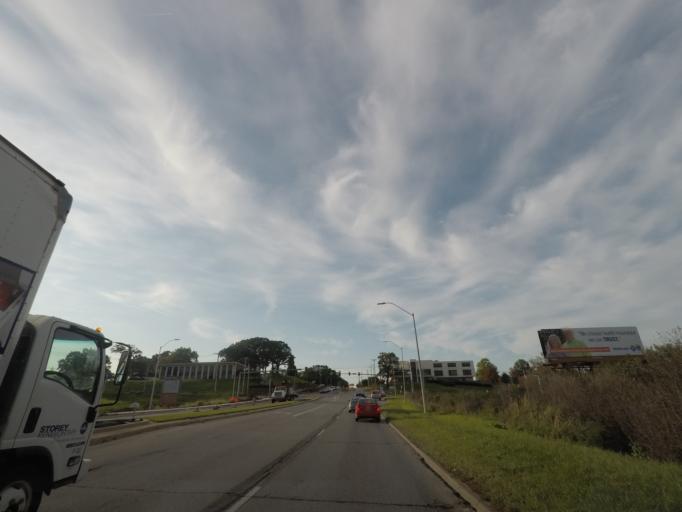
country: US
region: Iowa
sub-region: Polk County
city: Des Moines
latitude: 41.5638
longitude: -93.6451
